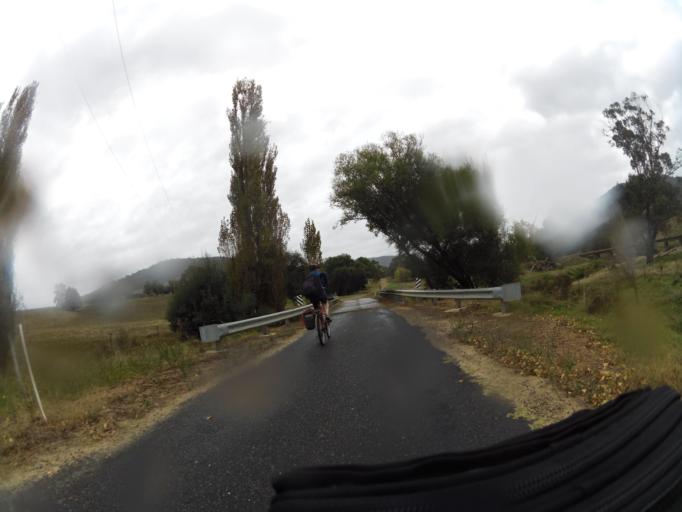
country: AU
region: New South Wales
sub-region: Greater Hume Shire
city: Holbrook
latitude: -36.2389
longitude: 147.6441
